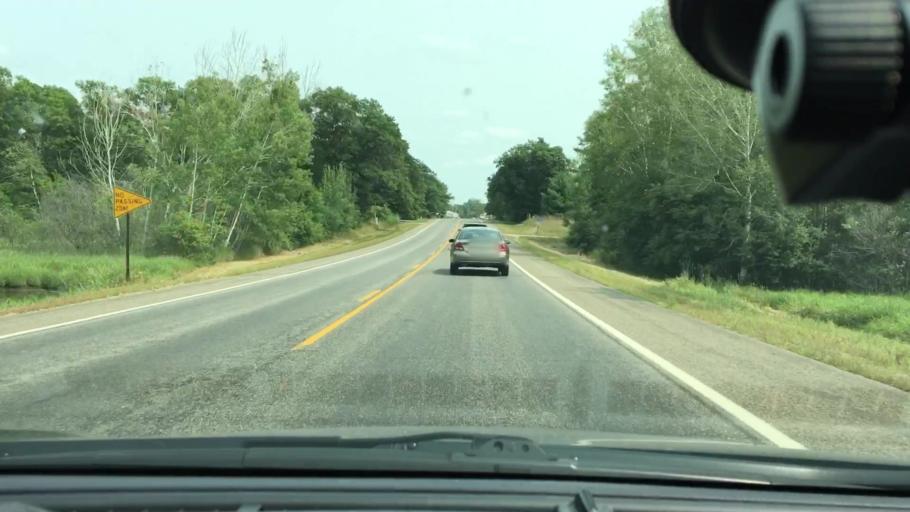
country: US
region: Minnesota
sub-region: Cass County
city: East Gull Lake
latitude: 46.4128
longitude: -94.2929
